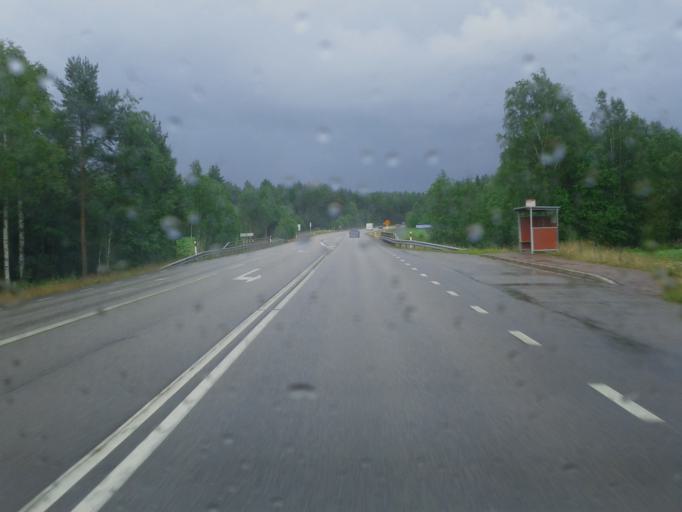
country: SE
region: Dalarna
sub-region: Rattviks Kommun
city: Vikarbyn
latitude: 60.9059
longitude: 14.9601
